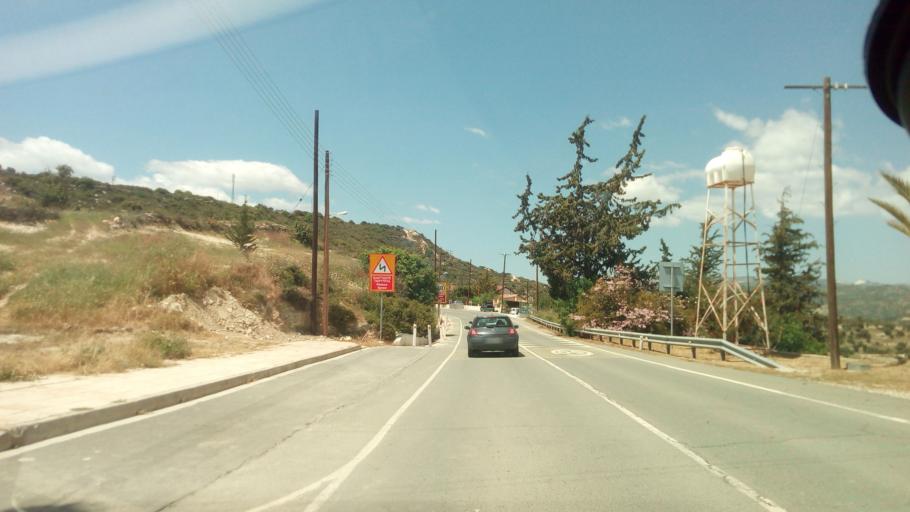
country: CY
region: Limassol
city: Sotira
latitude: 34.7612
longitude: 32.8445
